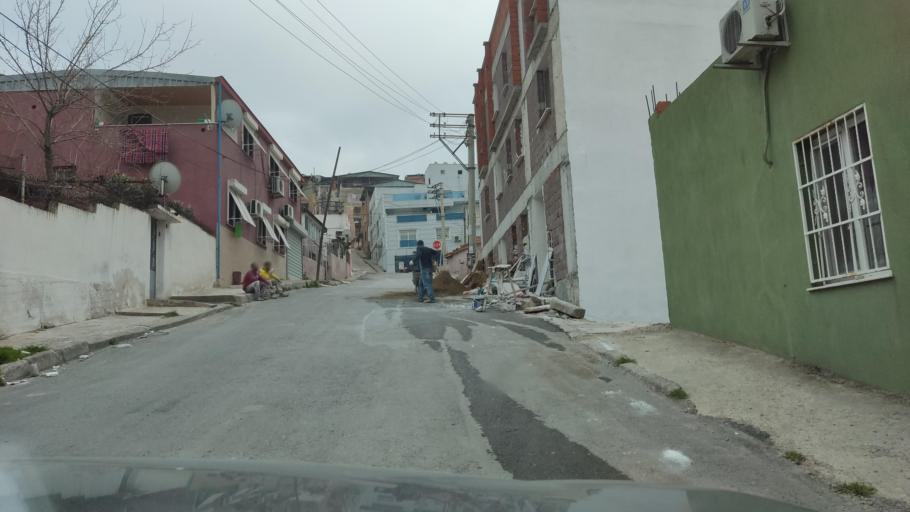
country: TR
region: Izmir
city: Karsiyaka
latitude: 38.5015
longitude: 27.0722
